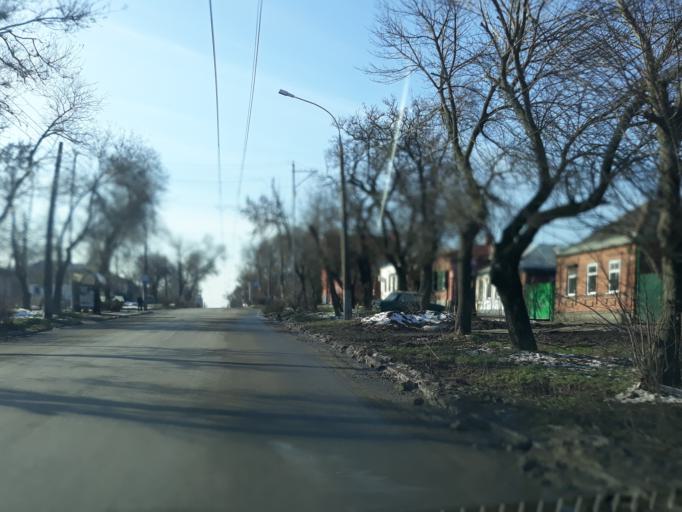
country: RU
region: Rostov
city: Taganrog
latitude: 47.2053
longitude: 38.9110
